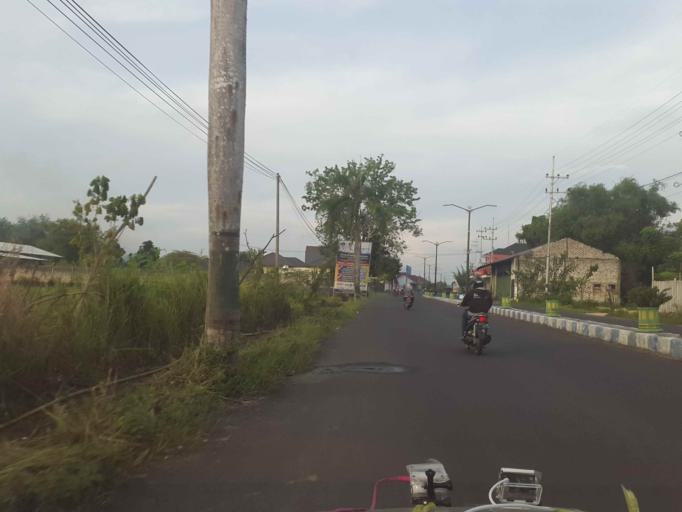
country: ID
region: East Java
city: Sumenep
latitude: -7.0316
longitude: 113.8517
